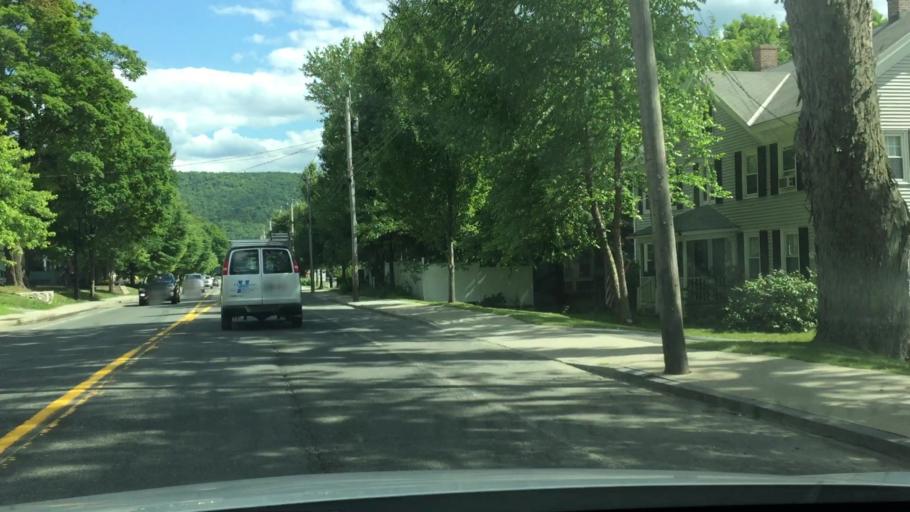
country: US
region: Massachusetts
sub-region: Berkshire County
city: Lee
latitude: 42.3027
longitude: -73.2444
